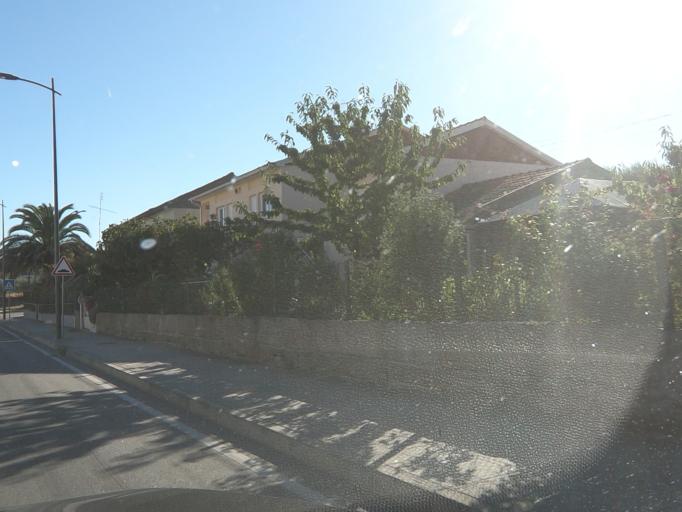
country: PT
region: Vila Real
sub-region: Valpacos
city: Valpacos
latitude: 41.6015
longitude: -7.3084
